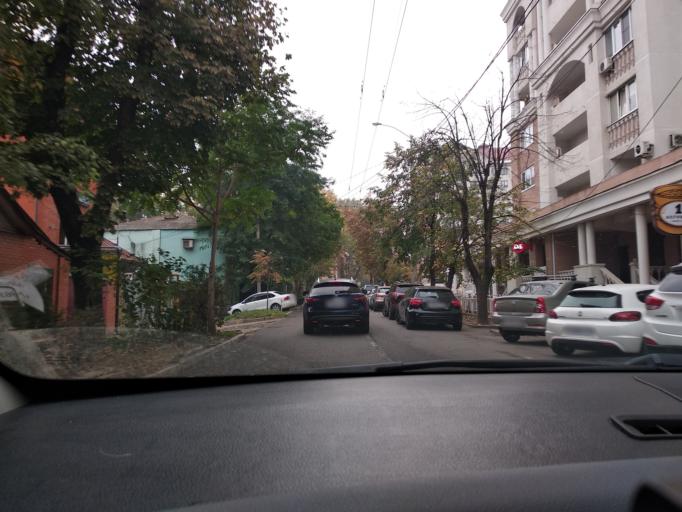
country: RU
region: Krasnodarskiy
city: Krasnodar
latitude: 45.0221
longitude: 38.9605
